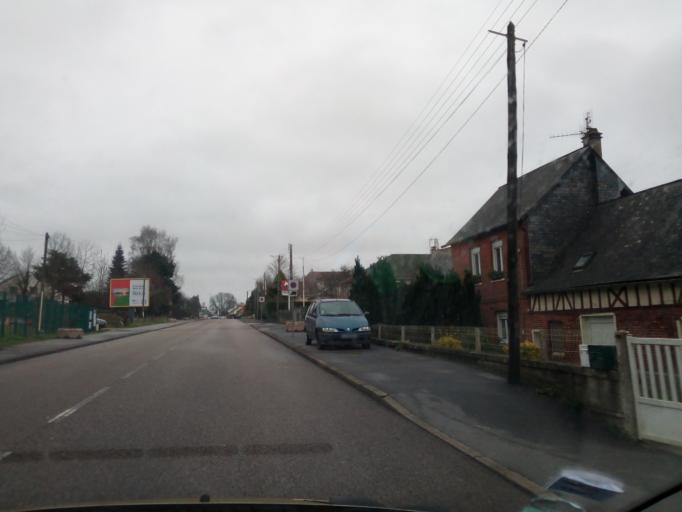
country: FR
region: Haute-Normandie
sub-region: Departement de la Seine-Maritime
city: Yvetot
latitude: 49.6104
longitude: 0.7455
